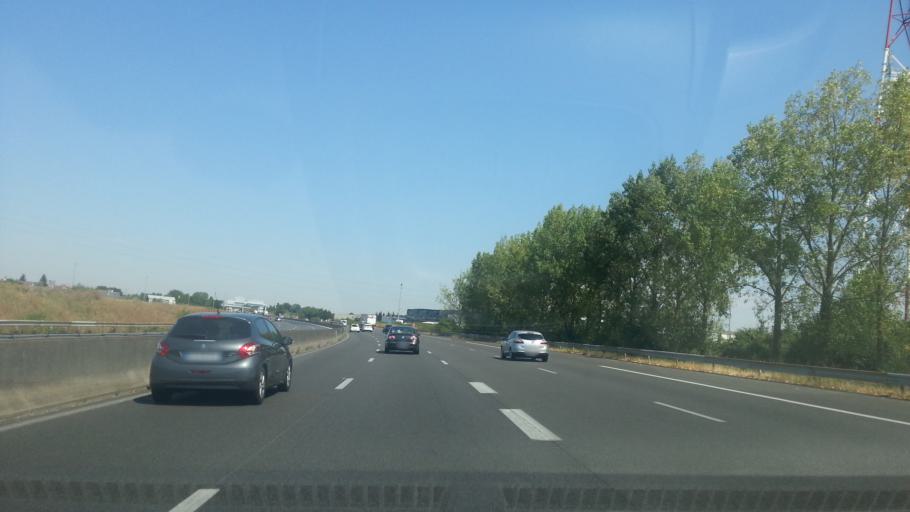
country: FR
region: Centre
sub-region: Departement du Loiret
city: Saint-Jean-de-la-Ruelle
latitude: 47.9066
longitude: 1.8495
